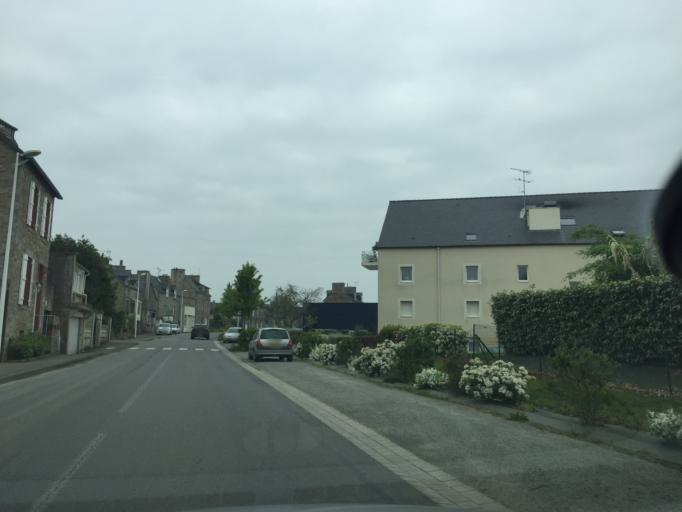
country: FR
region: Brittany
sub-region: Departement des Cotes-d'Armor
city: Matignon
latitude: 48.5975
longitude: -2.2866
